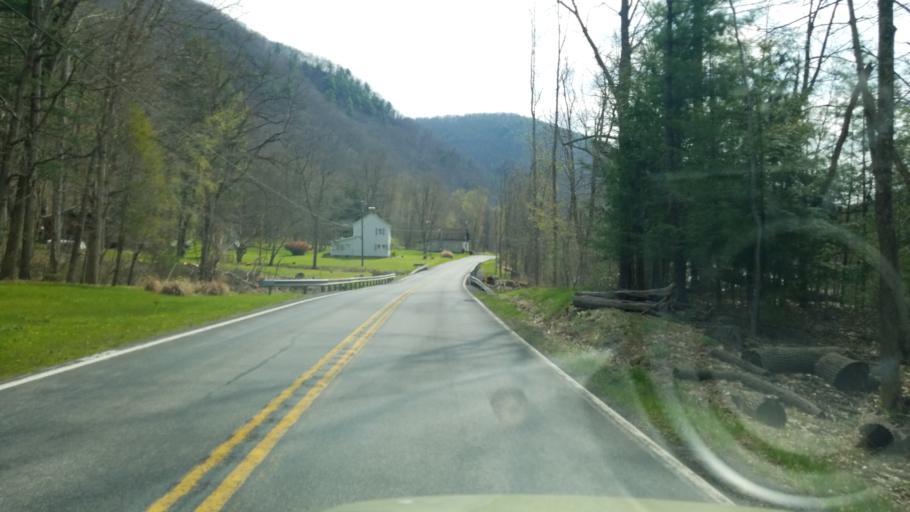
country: US
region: Pennsylvania
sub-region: Clinton County
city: Renovo
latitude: 41.3006
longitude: -77.9899
